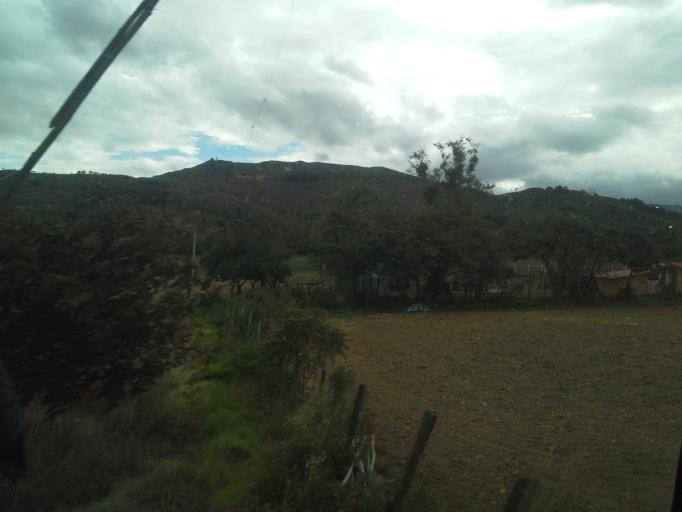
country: CO
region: Boyaca
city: Raquira
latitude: 5.5566
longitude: -73.6431
